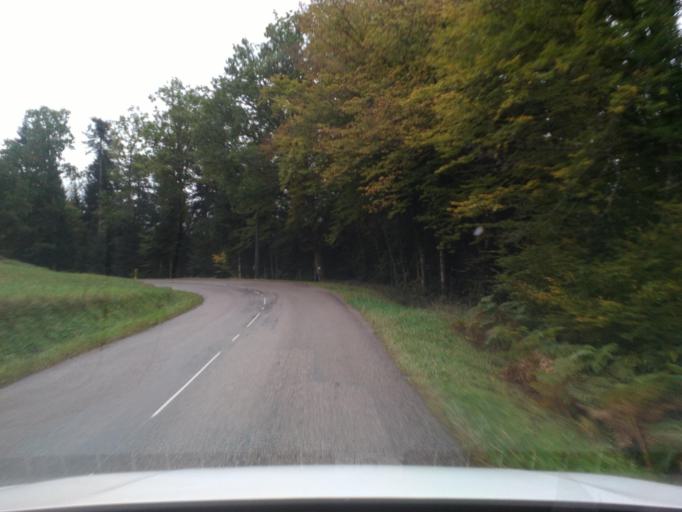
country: FR
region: Lorraine
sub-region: Departement des Vosges
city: Moyenmoutier
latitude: 48.3726
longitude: 6.9198
